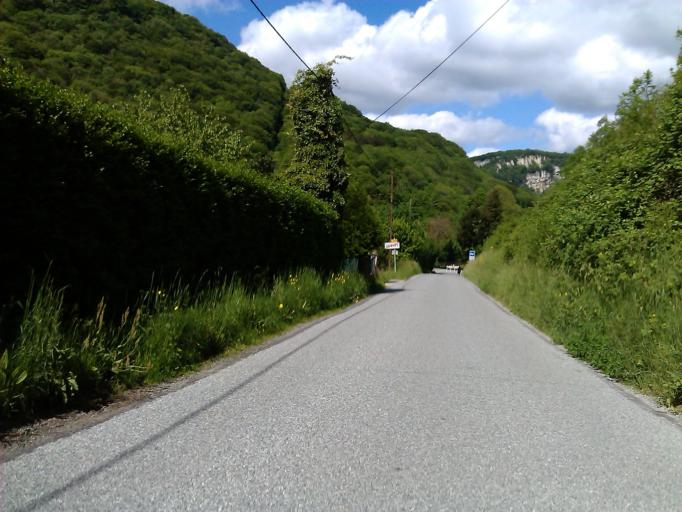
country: FR
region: Franche-Comte
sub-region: Departement du Doubs
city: Roulans
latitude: 47.2986
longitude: 6.2244
